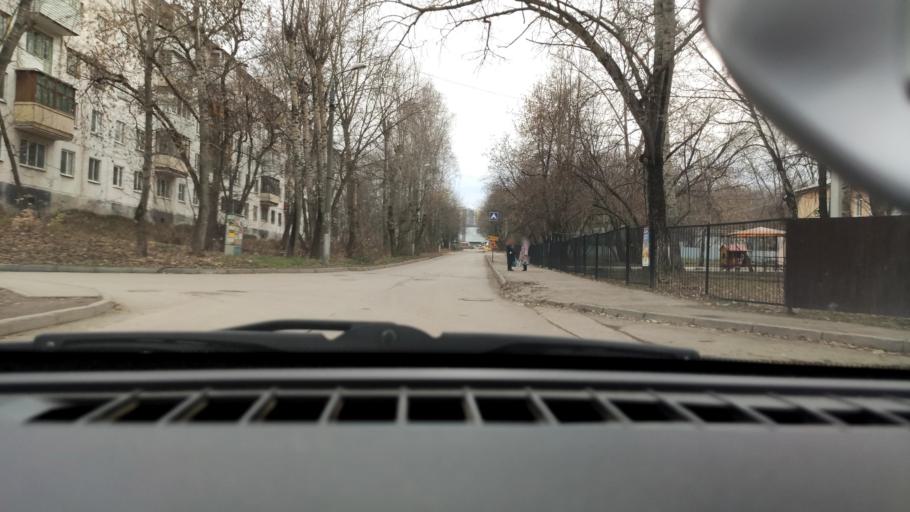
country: RU
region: Perm
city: Perm
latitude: 57.9970
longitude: 56.2135
